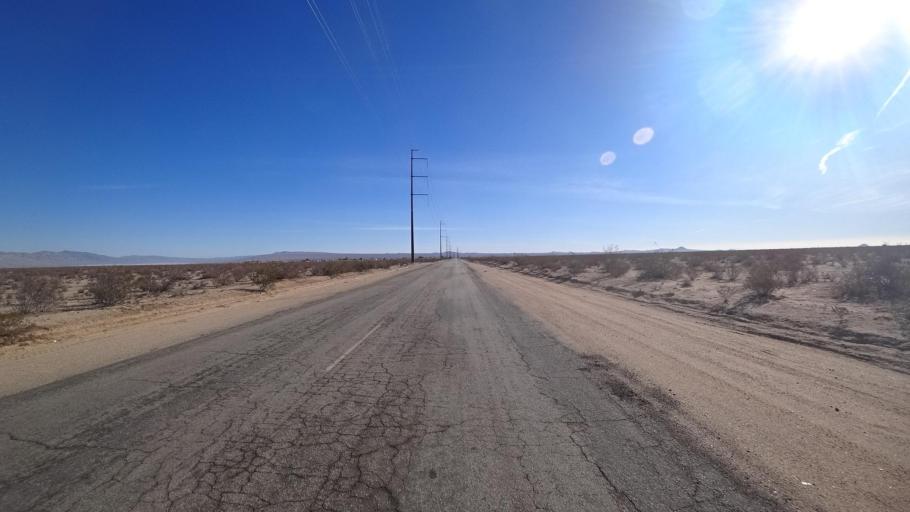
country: US
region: California
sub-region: Kern County
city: California City
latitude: 35.1986
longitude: -118.0321
